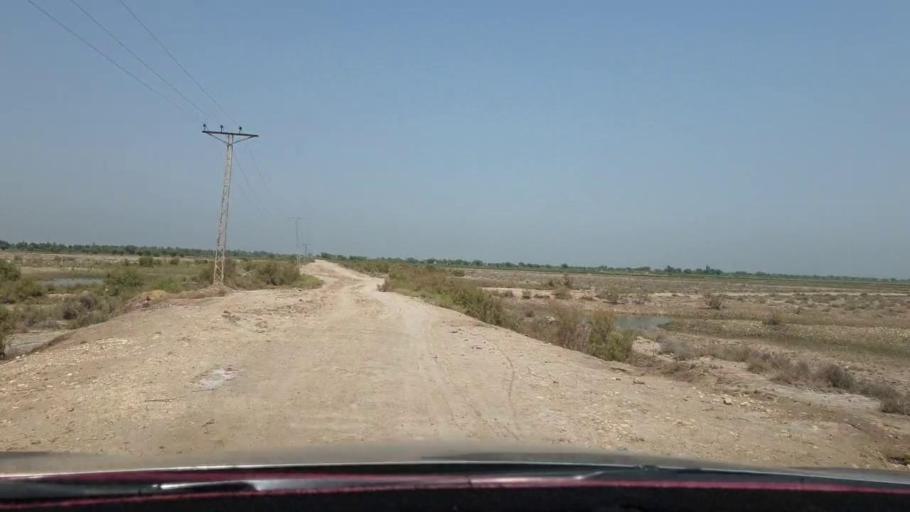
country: PK
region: Sindh
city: Warah
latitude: 27.3949
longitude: 67.6857
